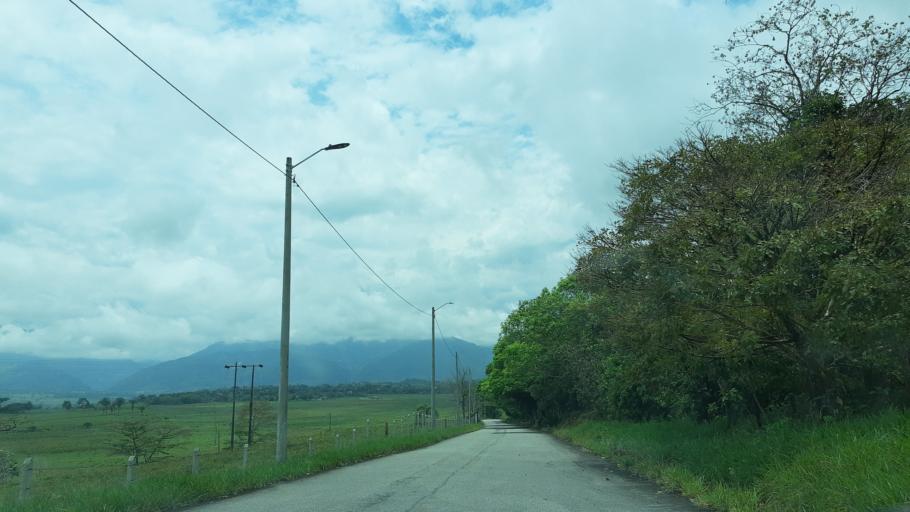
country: CO
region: Casanare
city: Sabanalarga
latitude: 4.8367
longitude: -73.0430
